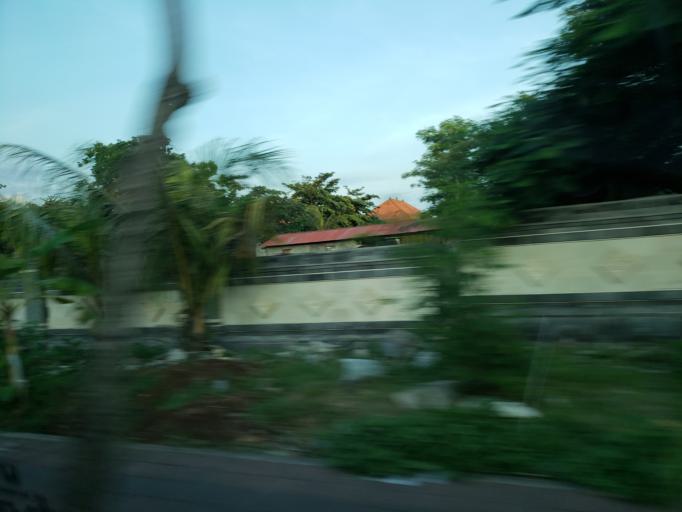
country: ID
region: Bali
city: Jimbaran
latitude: -8.8005
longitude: 115.1606
